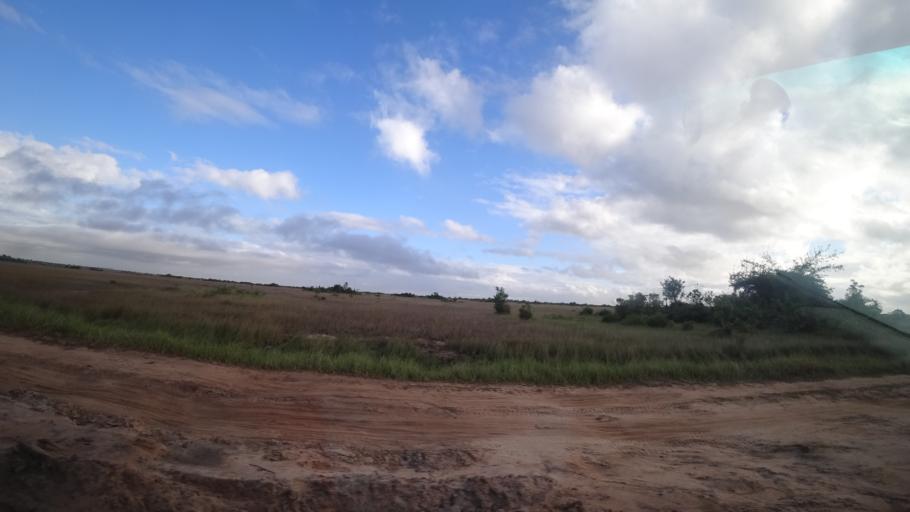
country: MZ
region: Sofala
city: Beira
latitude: -19.7028
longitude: 35.0234
